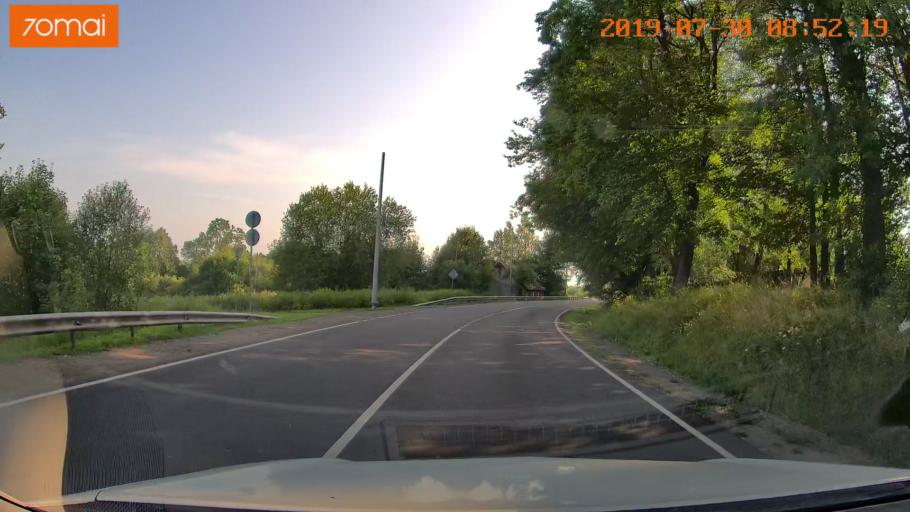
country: RU
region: Kaliningrad
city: Chernyakhovsk
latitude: 54.6018
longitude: 21.9715
